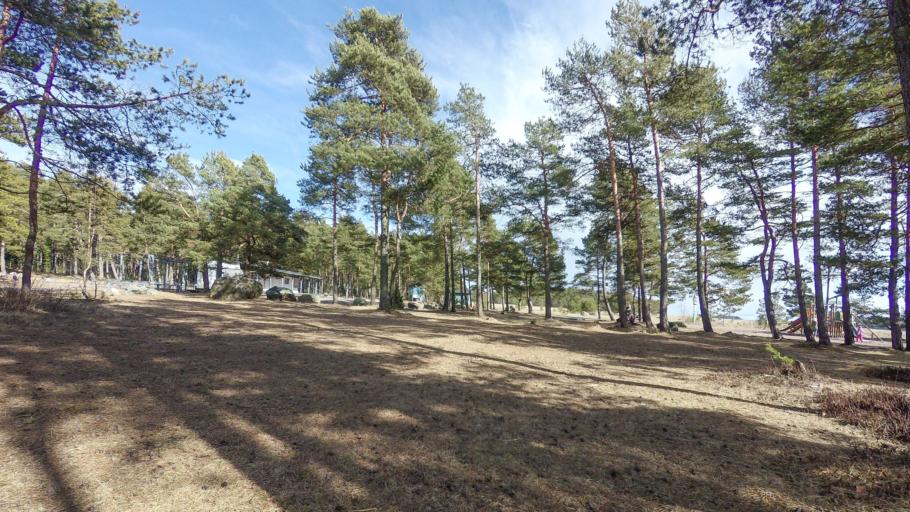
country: FI
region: Uusimaa
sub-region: Helsinki
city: Vantaa
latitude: 60.1872
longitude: 25.1436
